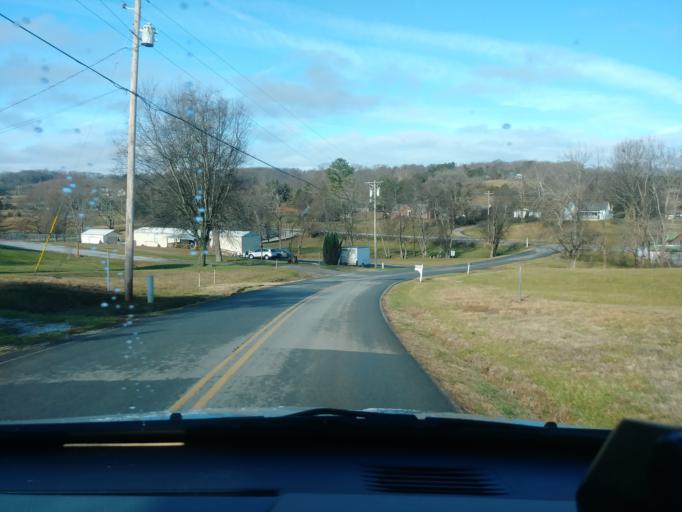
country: US
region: Tennessee
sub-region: Greene County
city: Mosheim
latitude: 36.0991
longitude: -82.9262
